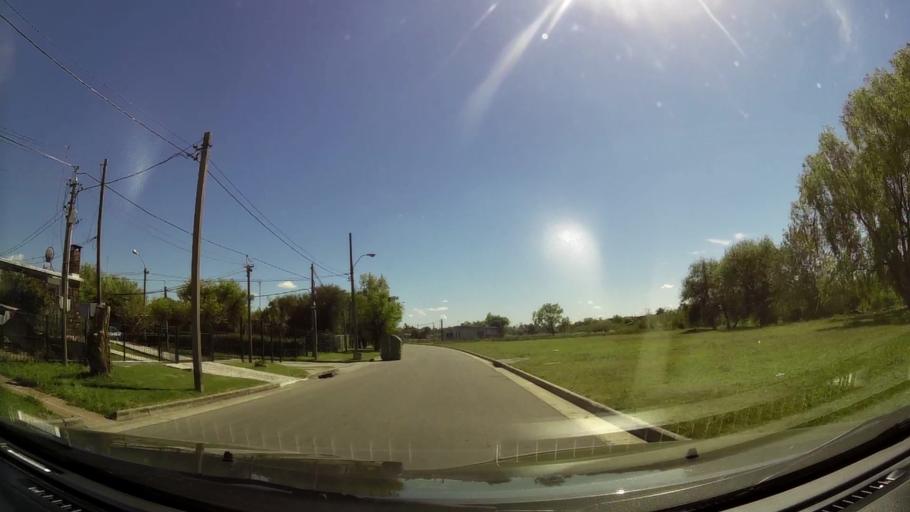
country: UY
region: Canelones
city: Paso de Carrasco
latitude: -34.8595
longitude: -56.1184
